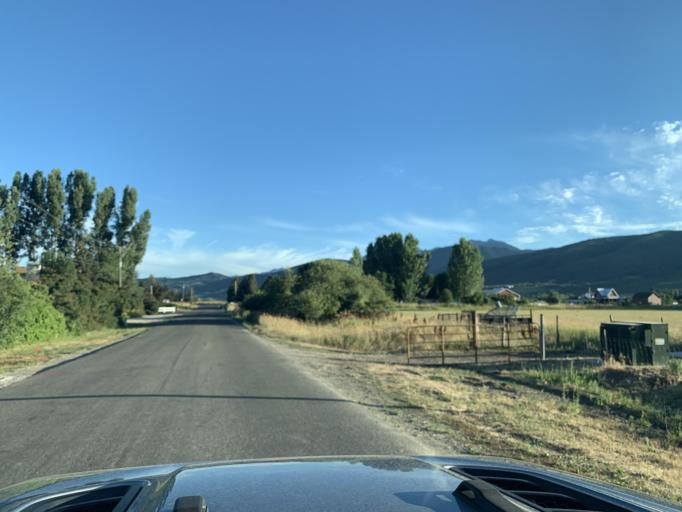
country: US
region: Utah
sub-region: Weber County
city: Wolf Creek
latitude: 41.2961
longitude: -111.8104
